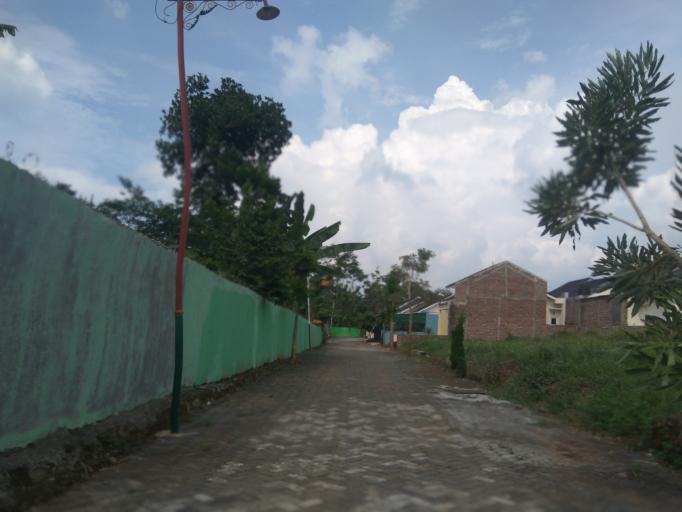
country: ID
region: Central Java
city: Ungaran
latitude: -7.0703
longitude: 110.4462
